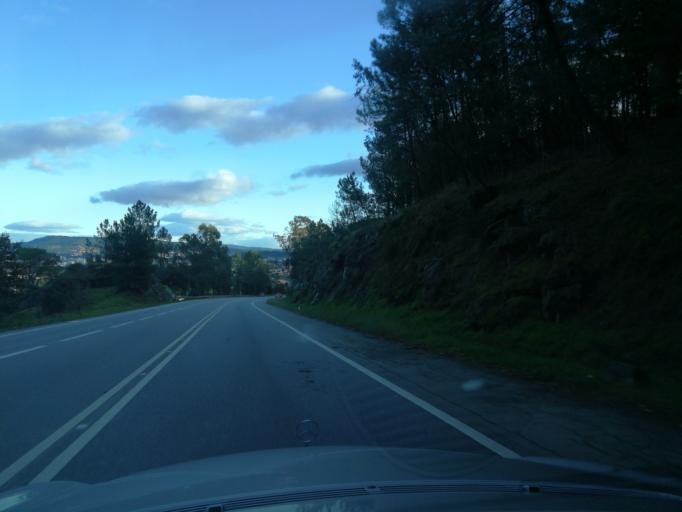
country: PT
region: Braga
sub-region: Barcelos
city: Vila Frescainha
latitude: 41.5406
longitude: -8.6427
